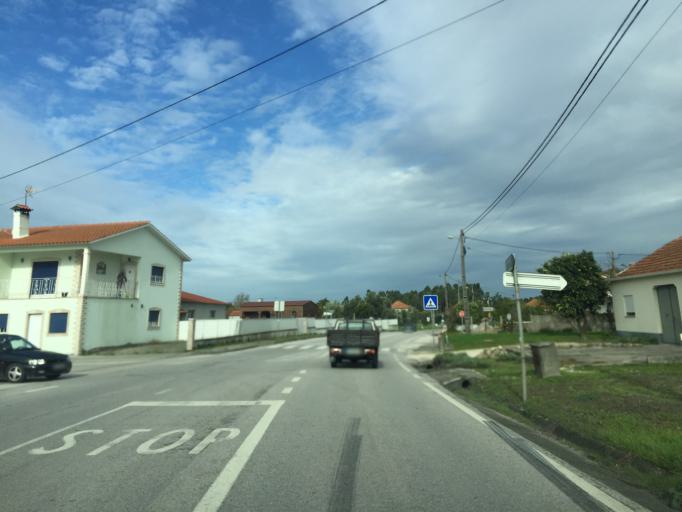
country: PT
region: Leiria
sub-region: Pombal
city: Lourical
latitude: 39.9690
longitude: -8.7926
